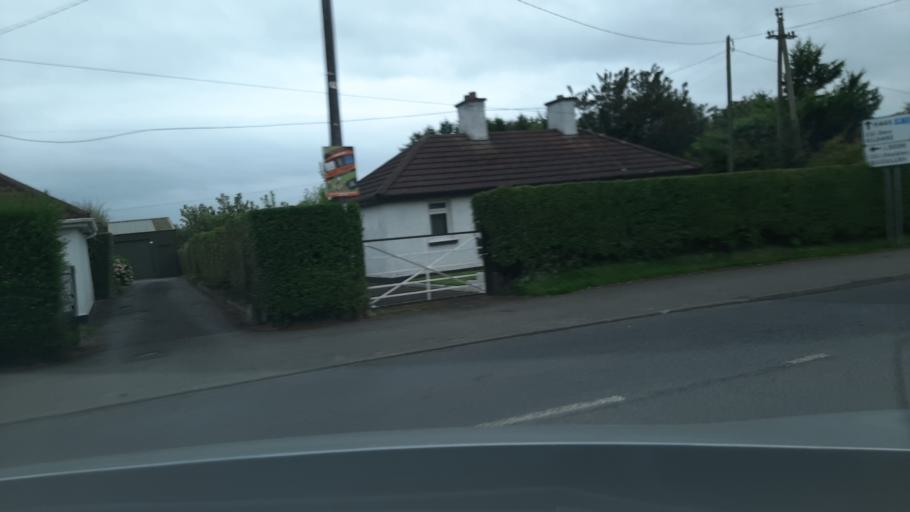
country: IE
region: Leinster
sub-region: Kildare
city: Kildare
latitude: 53.1549
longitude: -6.8927
